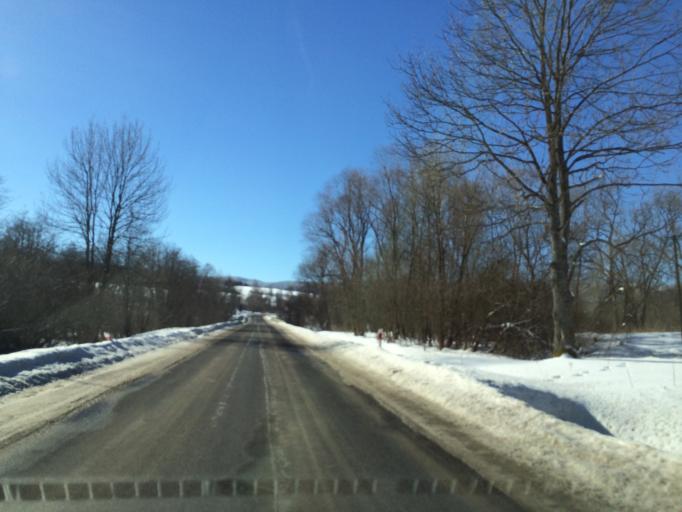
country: PL
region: Subcarpathian Voivodeship
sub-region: Powiat bieszczadzki
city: Lutowiska
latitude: 49.1139
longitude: 22.6623
